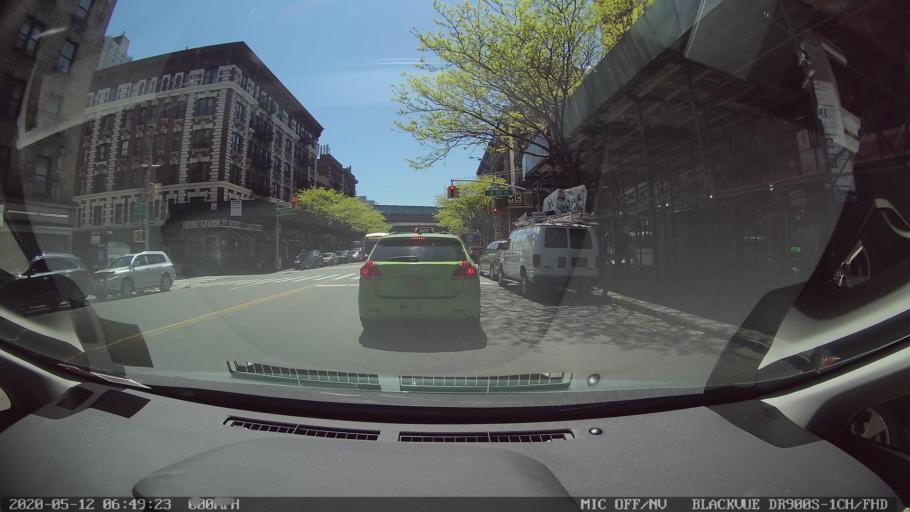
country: US
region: New York
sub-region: New York County
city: Inwood
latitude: 40.8497
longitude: -73.9362
